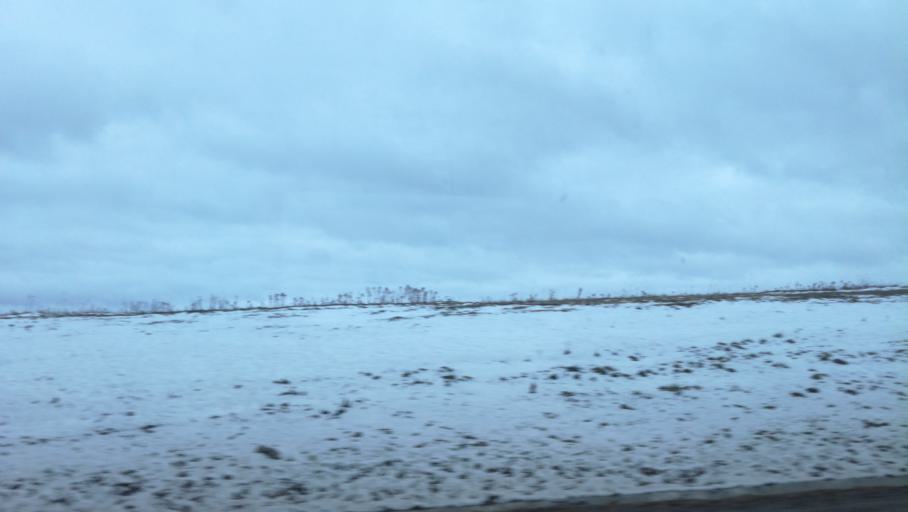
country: RU
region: Tula
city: Kosaya Gora
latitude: 54.1684
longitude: 37.4605
